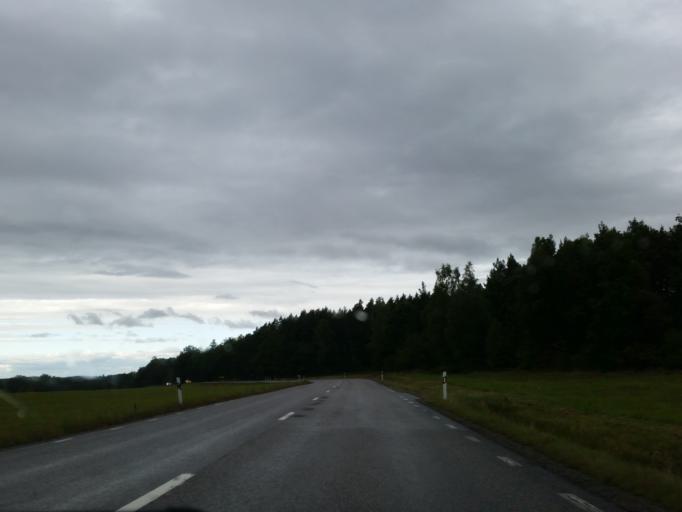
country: SE
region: Uppsala
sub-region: Habo Kommun
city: Balsta
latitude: 59.6487
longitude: 17.4248
